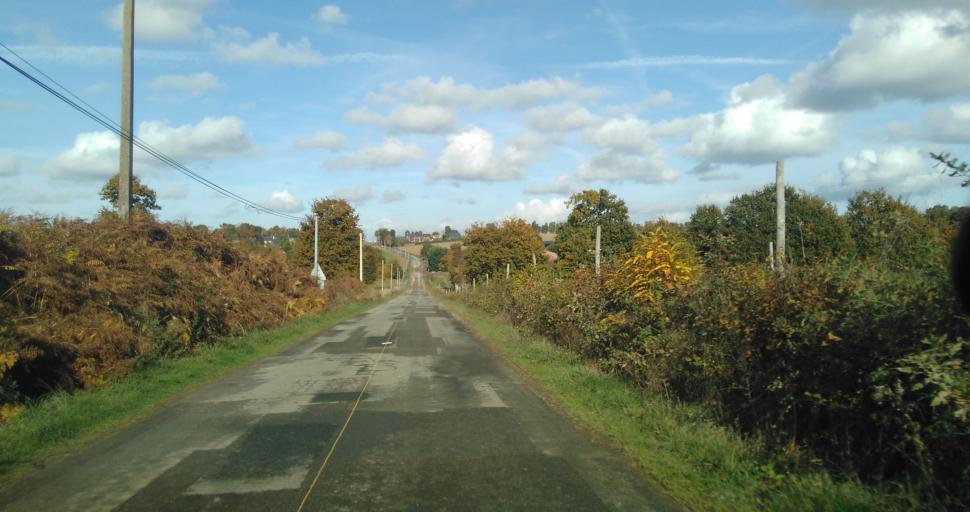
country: FR
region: Brittany
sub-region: Departement d'Ille-et-Vilaine
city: Iffendic
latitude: 48.1122
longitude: -2.0869
